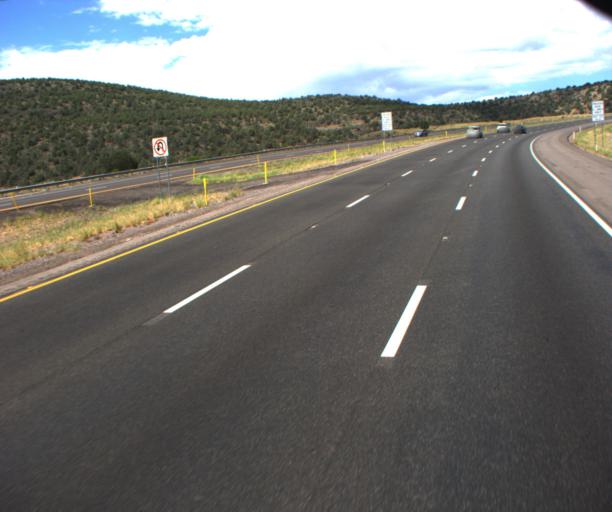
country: US
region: Arizona
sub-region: Yavapai County
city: Camp Verde
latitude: 34.5304
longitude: -111.9472
